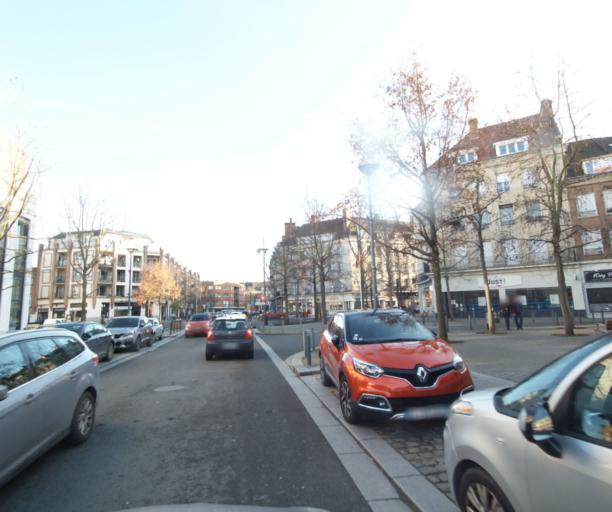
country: FR
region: Nord-Pas-de-Calais
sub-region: Departement du Nord
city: Valenciennes
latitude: 50.3601
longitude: 3.5242
